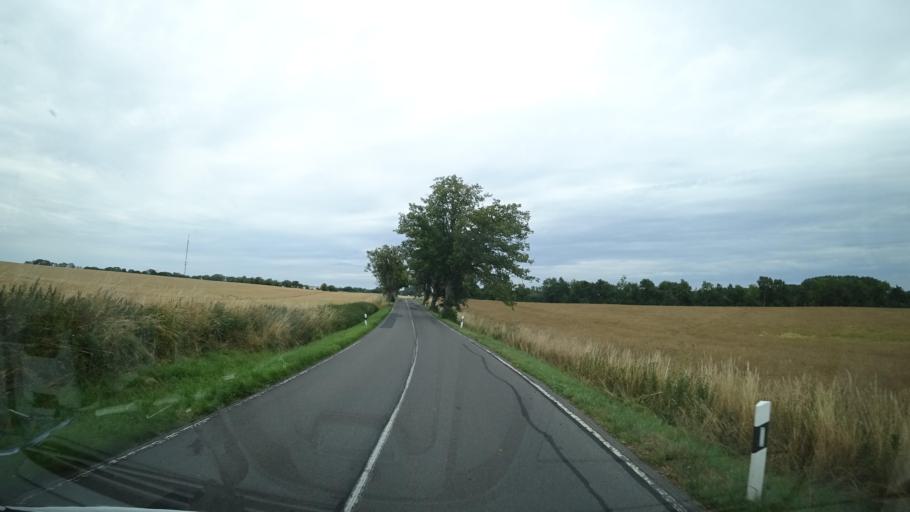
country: DE
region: Mecklenburg-Vorpommern
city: Garz
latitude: 54.3109
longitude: 13.3312
